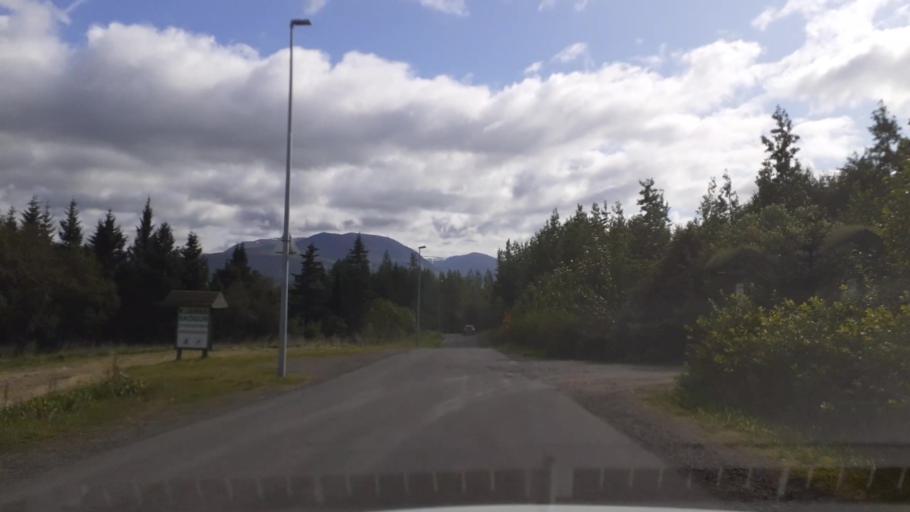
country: IS
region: Northeast
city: Akureyri
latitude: 65.6483
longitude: -18.0876
